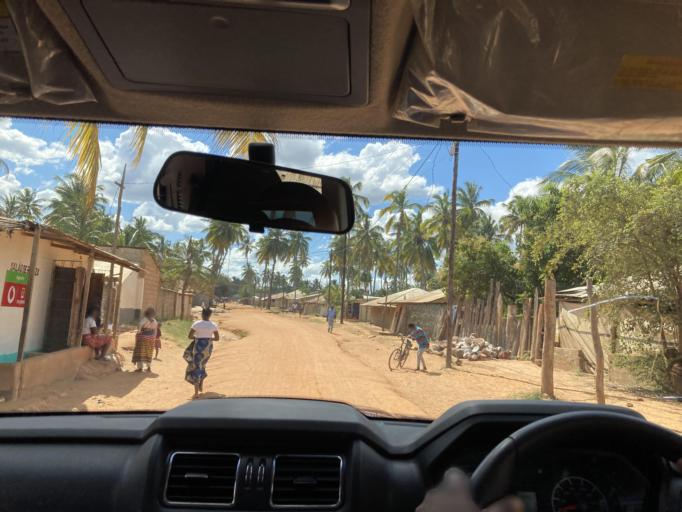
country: MZ
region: Cabo Delgado
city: Montepuez
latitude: -13.1325
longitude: 39.0059
